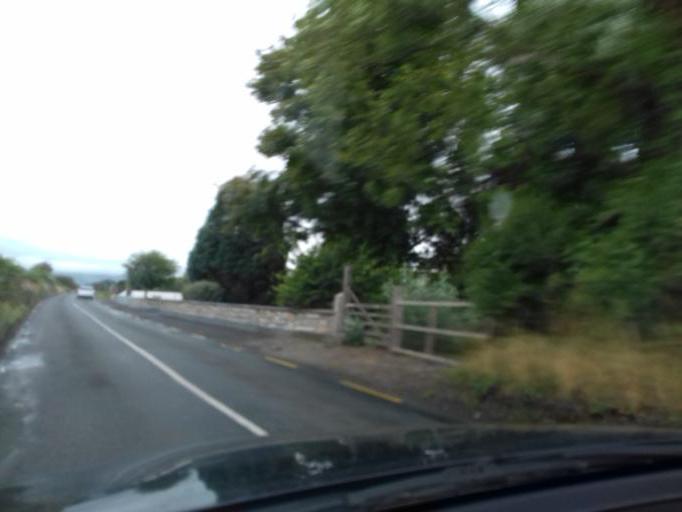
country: IE
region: Leinster
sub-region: County Carlow
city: Bagenalstown
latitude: 52.7277
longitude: -6.9703
